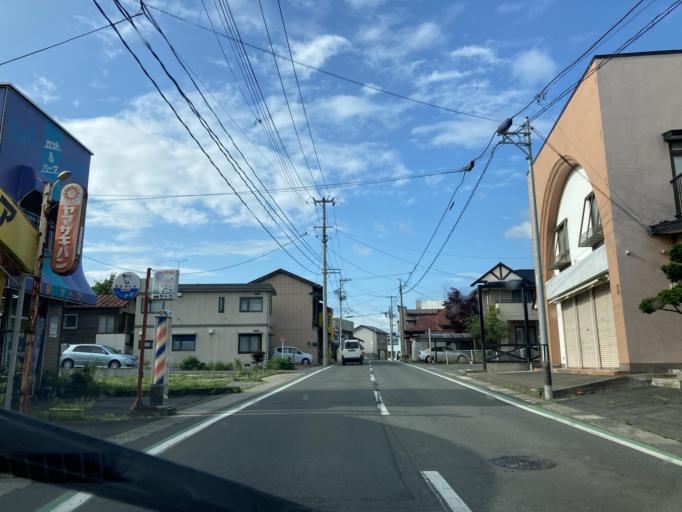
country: JP
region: Iwate
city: Ichinohe
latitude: 39.9679
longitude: 141.2213
